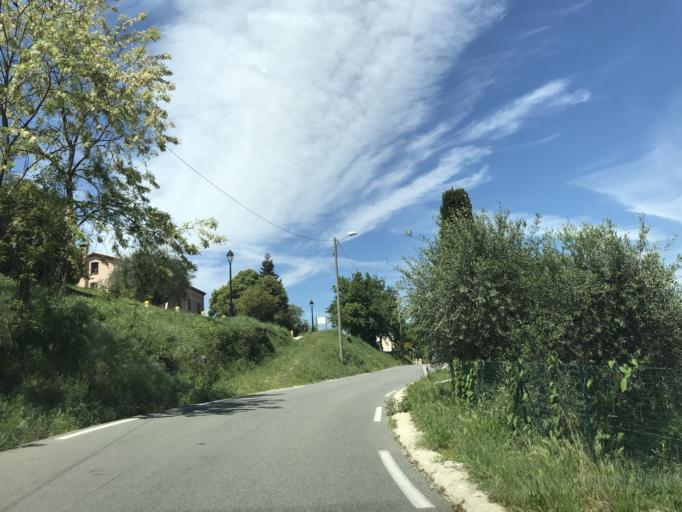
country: FR
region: Provence-Alpes-Cote d'Azur
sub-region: Departement du Var
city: Tanneron
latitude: 43.5895
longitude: 6.8769
